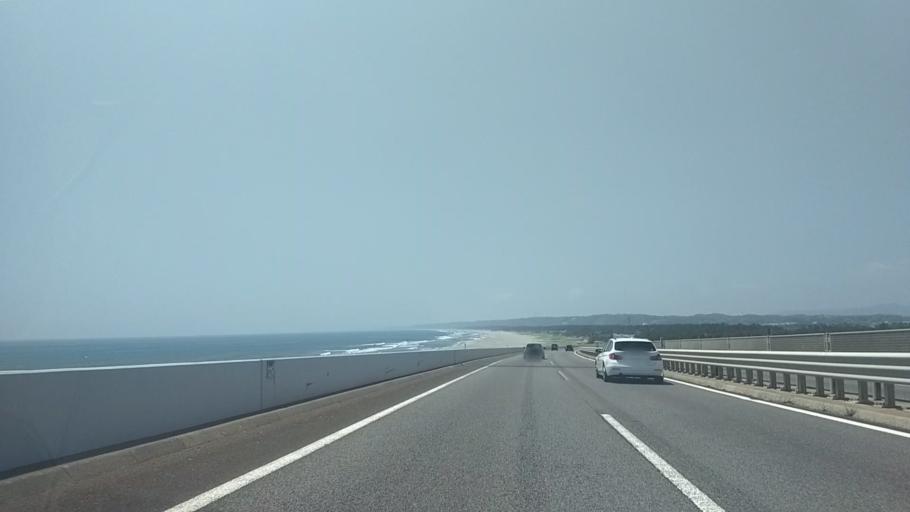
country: JP
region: Shizuoka
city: Kosai-shi
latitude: 34.6792
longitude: 137.5921
